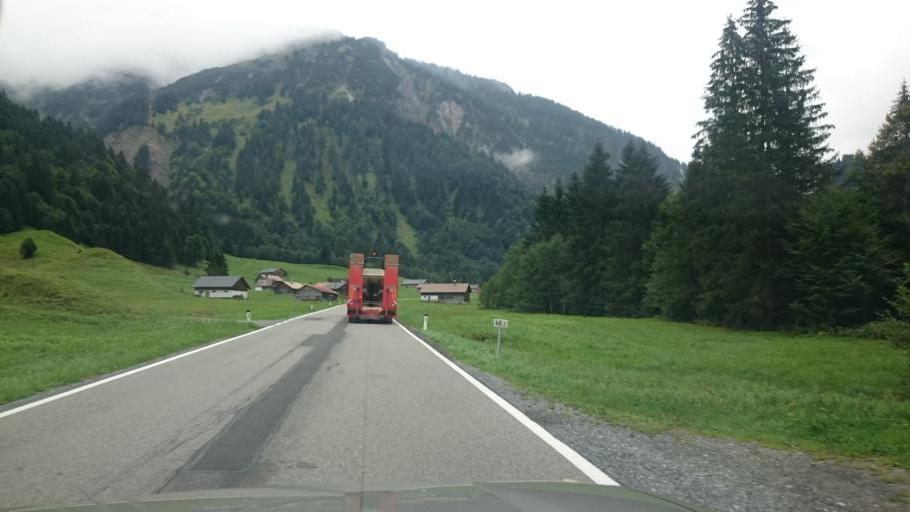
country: AT
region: Vorarlberg
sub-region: Politischer Bezirk Bregenz
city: Schoppernau
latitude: 47.2844
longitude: 10.0522
